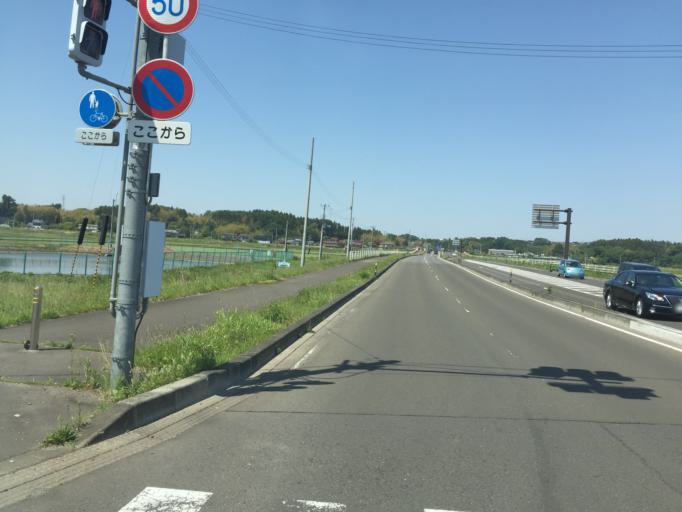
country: JP
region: Miyagi
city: Iwanuma
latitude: 38.1448
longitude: 140.8617
